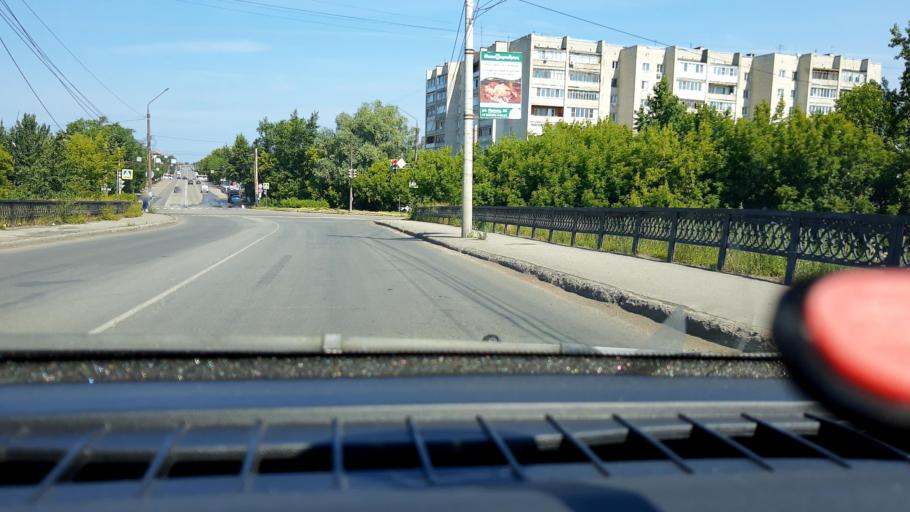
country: RU
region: Nizjnij Novgorod
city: Dzerzhinsk
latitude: 56.2359
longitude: 43.4883
